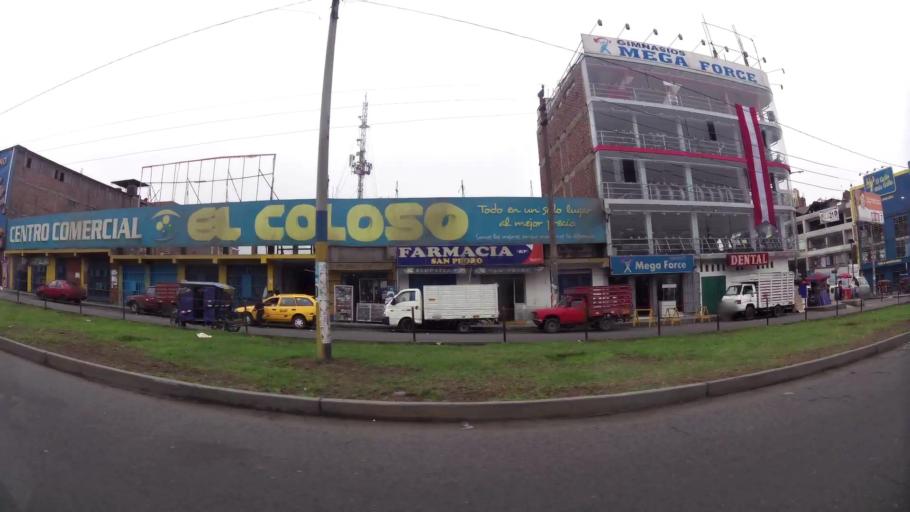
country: PE
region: Lima
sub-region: Lima
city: Independencia
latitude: -11.9473
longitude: -76.9847
